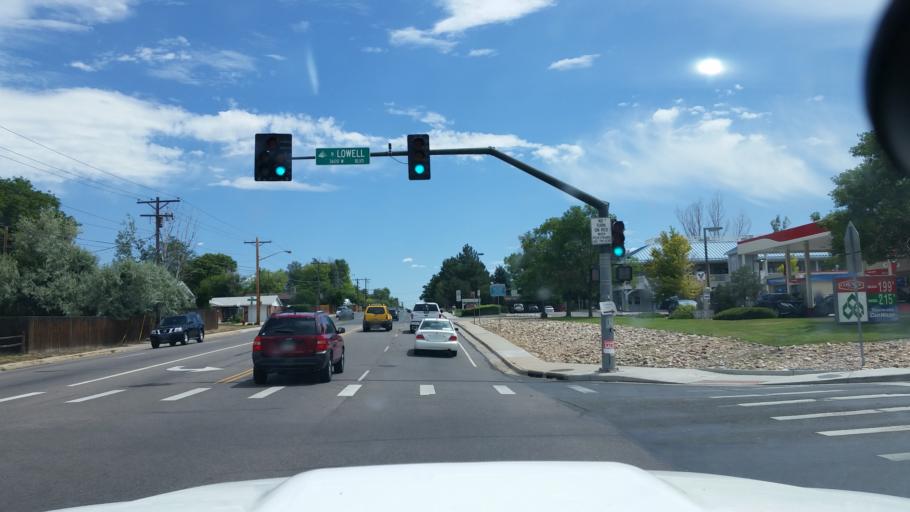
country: US
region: Colorado
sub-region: Adams County
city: Westminster
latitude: 39.8634
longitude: -105.0346
